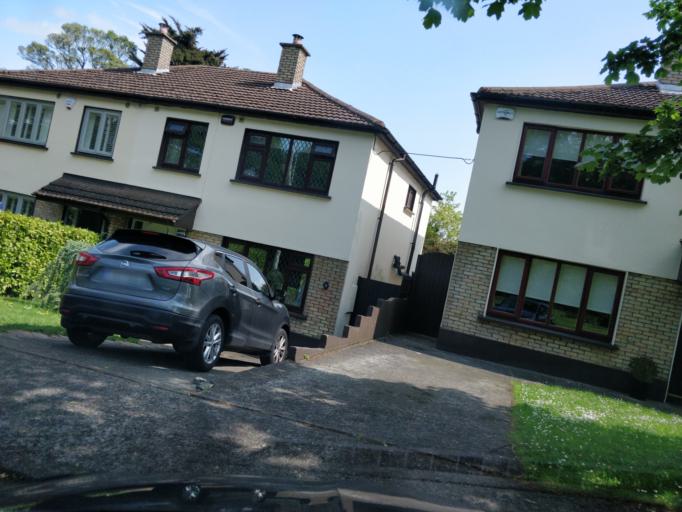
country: IE
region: Leinster
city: Balally
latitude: 53.2913
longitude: -6.2326
